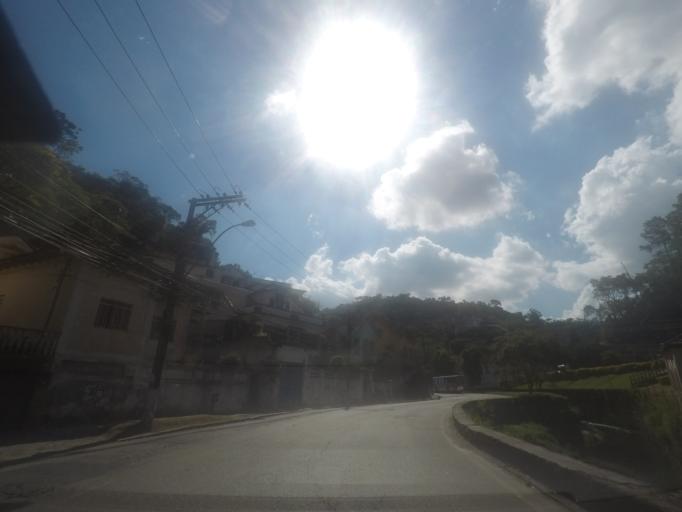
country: BR
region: Rio de Janeiro
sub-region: Petropolis
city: Petropolis
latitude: -22.5167
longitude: -43.1841
